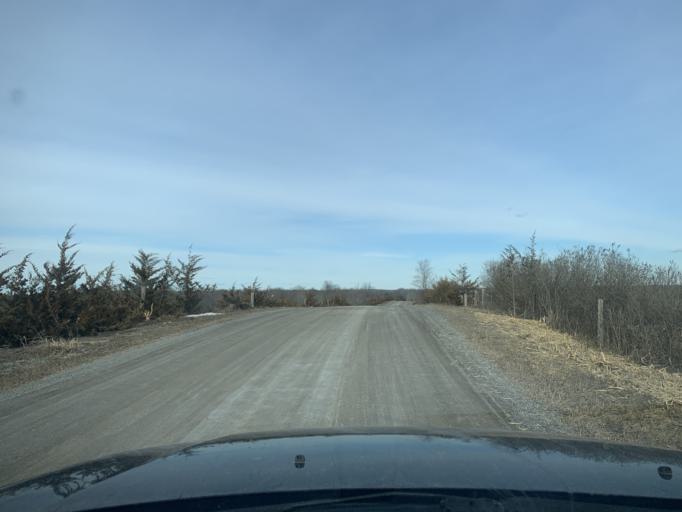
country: CA
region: Ontario
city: Deseronto
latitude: 44.4016
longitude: -77.1312
